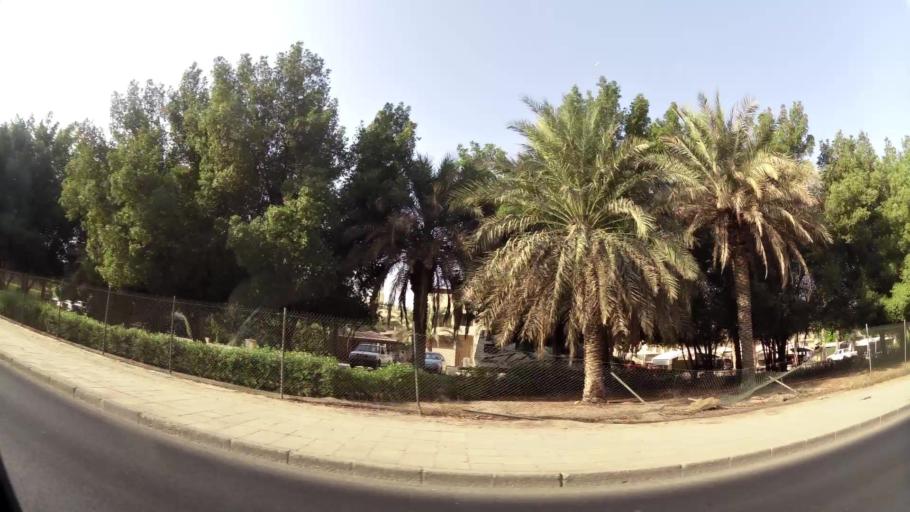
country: KW
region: Muhafazat Hawalli
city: Hawalli
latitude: 29.3516
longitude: 48.0268
